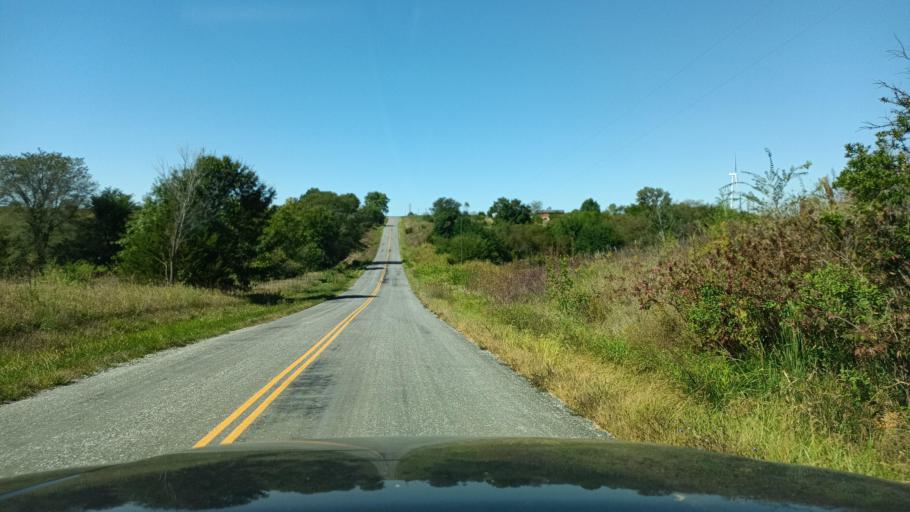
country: US
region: Missouri
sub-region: Adair County
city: Kirksville
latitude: 40.3304
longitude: -92.5183
